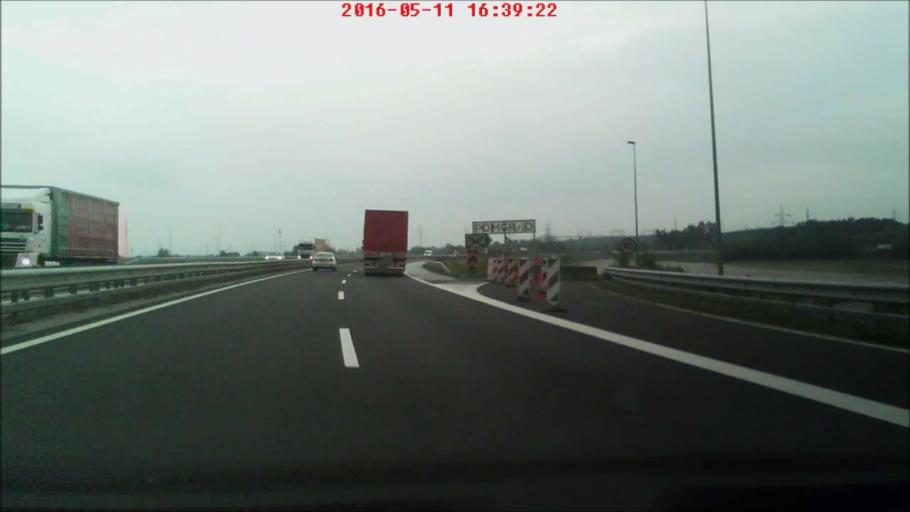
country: SI
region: Miklavz na Dravskem Polju
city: Miklavz na Dravskem Polju
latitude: 46.5369
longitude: 15.6992
